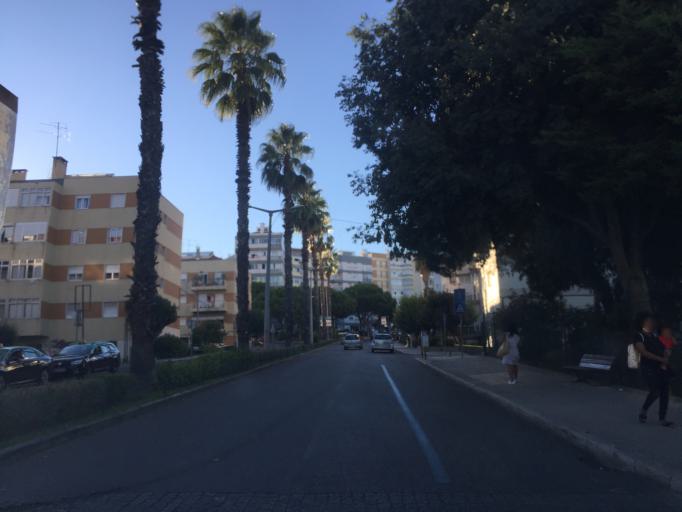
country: PT
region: Lisbon
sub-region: Odivelas
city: Povoa de Santo Adriao
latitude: 38.7978
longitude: -9.1623
